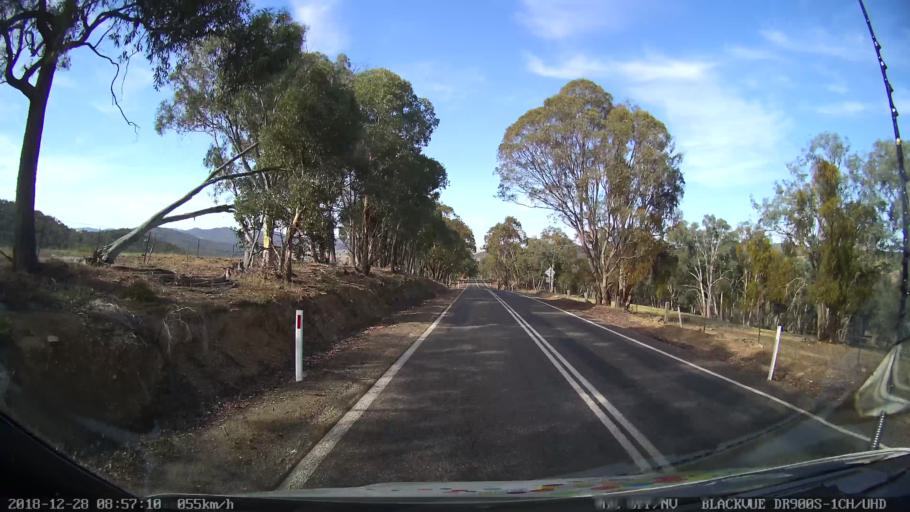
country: AU
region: New South Wales
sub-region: Upper Lachlan Shire
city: Crookwell
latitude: -34.1169
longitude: 149.3371
